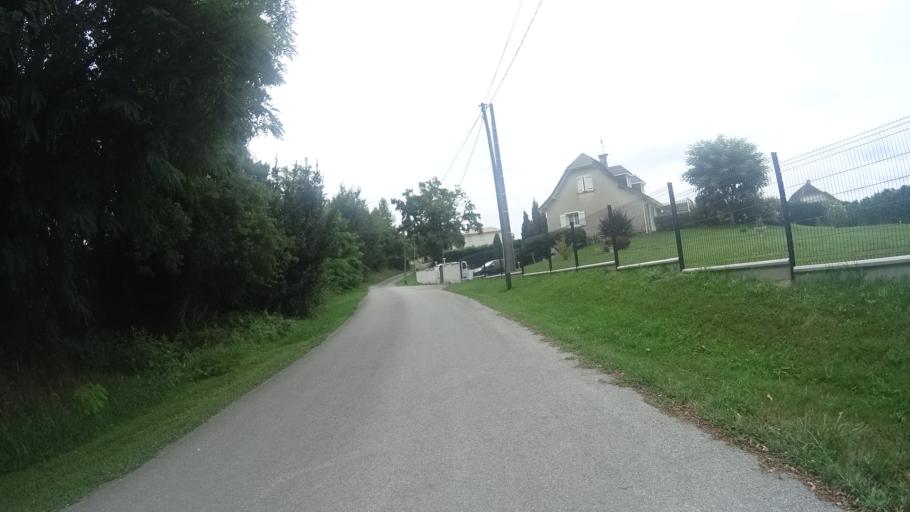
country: FR
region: Aquitaine
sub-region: Departement des Pyrenees-Atlantiques
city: Mont
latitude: 43.4806
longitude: -0.6989
